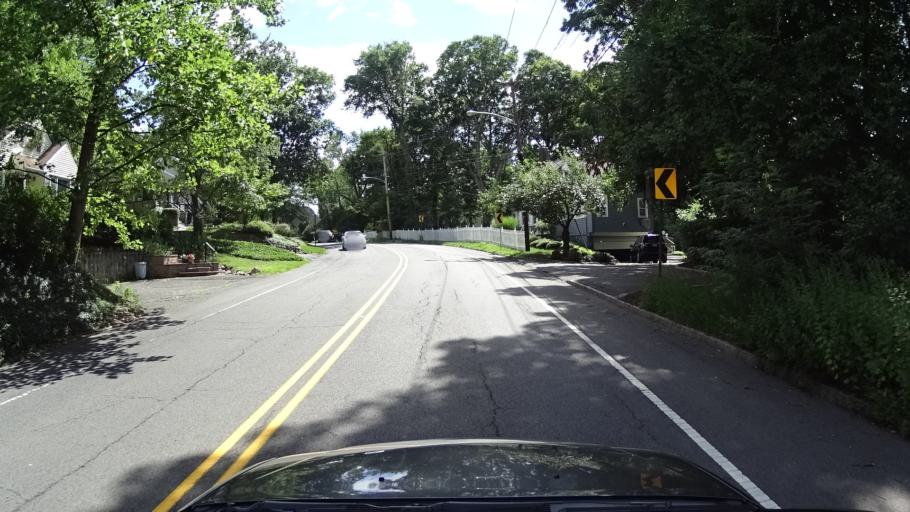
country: US
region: New Jersey
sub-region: Morris County
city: Chatham
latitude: 40.7245
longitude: -74.3833
